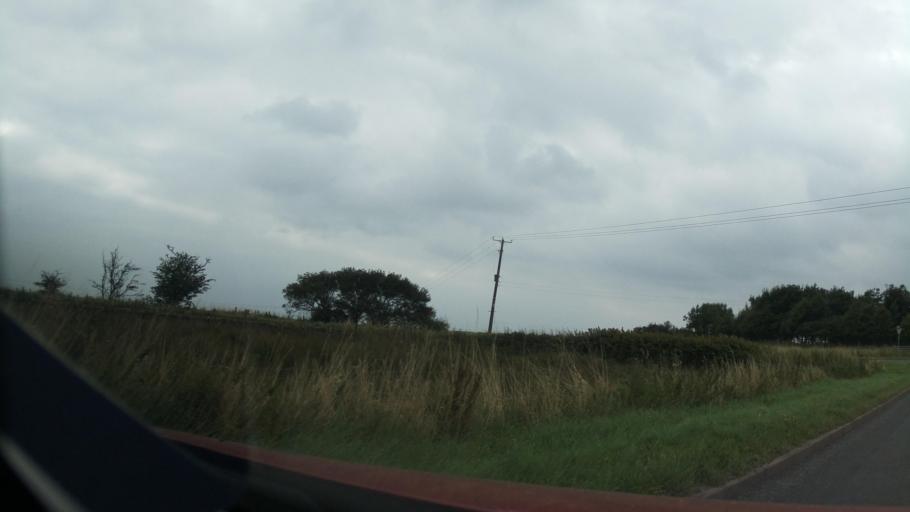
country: GB
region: England
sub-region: Staffordshire
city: Cheadle
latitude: 53.0309
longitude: -1.9029
